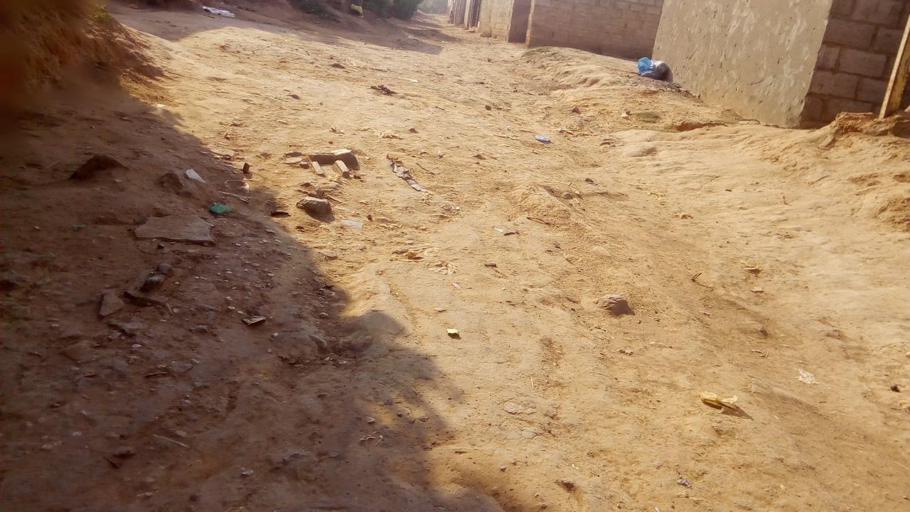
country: ZM
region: Lusaka
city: Lusaka
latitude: -15.3603
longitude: 28.2894
